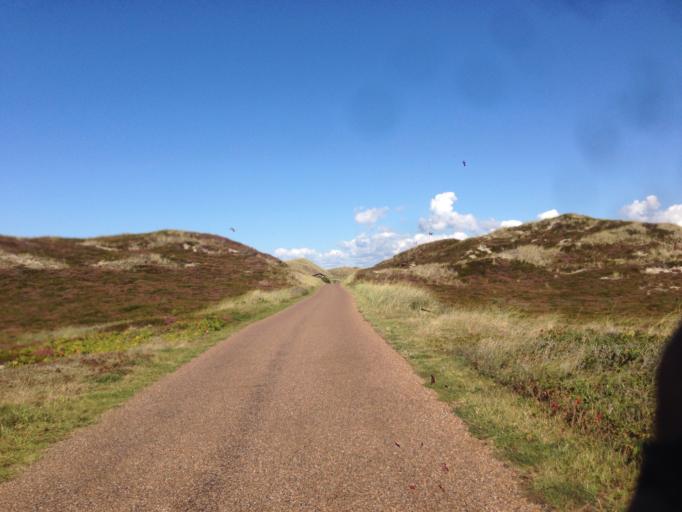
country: DE
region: Schleswig-Holstein
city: List
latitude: 54.9994
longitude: 8.3640
